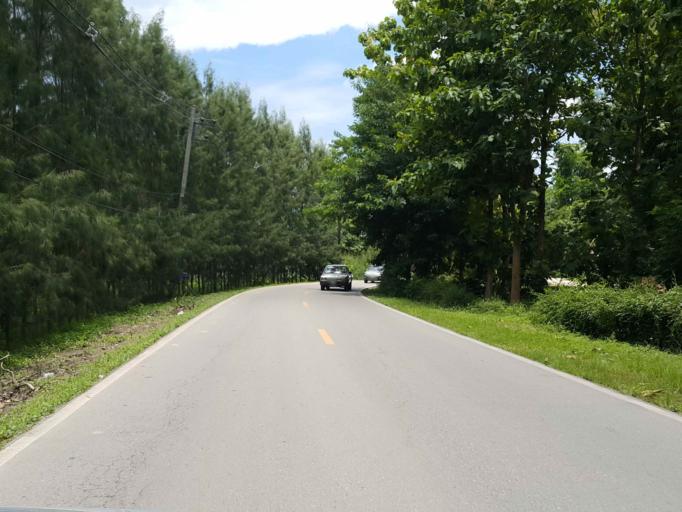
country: TH
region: Chiang Mai
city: San Sai
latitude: 18.8550
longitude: 98.9861
